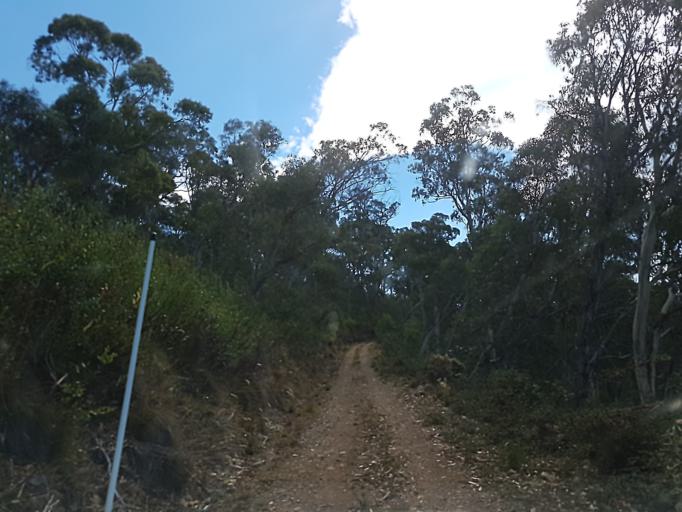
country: AU
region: Victoria
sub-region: Alpine
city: Mount Beauty
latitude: -36.9119
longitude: 147.0045
